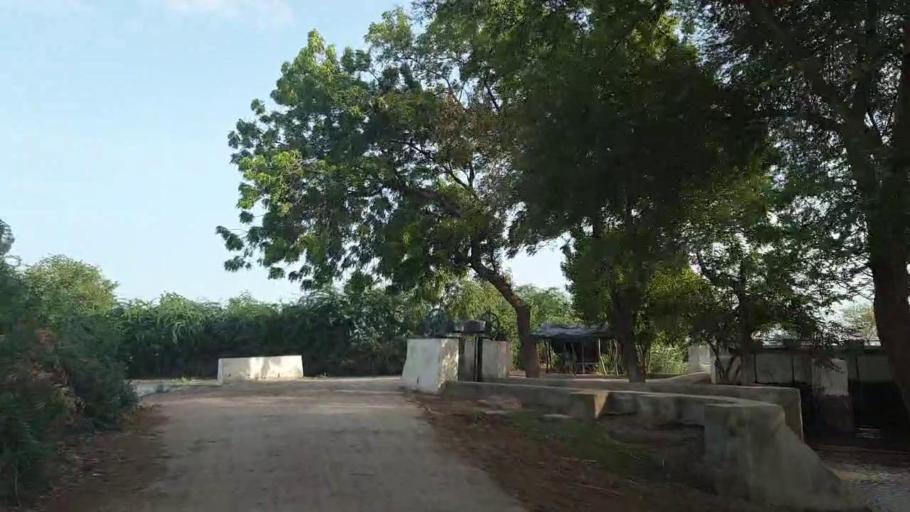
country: PK
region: Sindh
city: Kadhan
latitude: 24.6393
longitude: 69.1039
